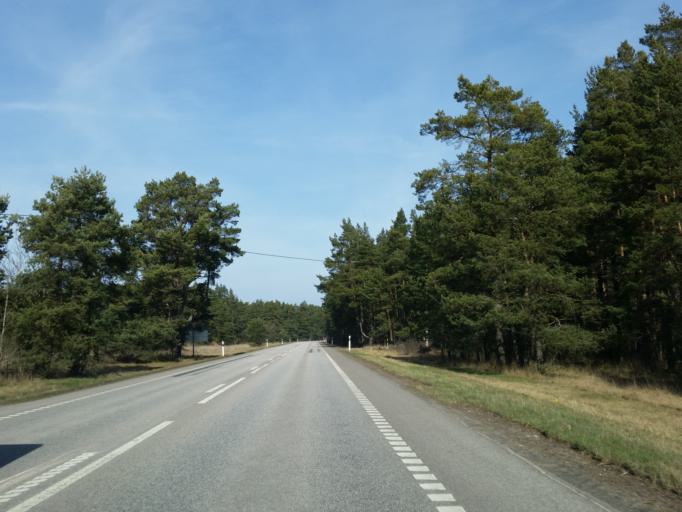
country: SE
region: Kalmar
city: Faerjestaden
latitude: 56.7464
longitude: 16.5479
